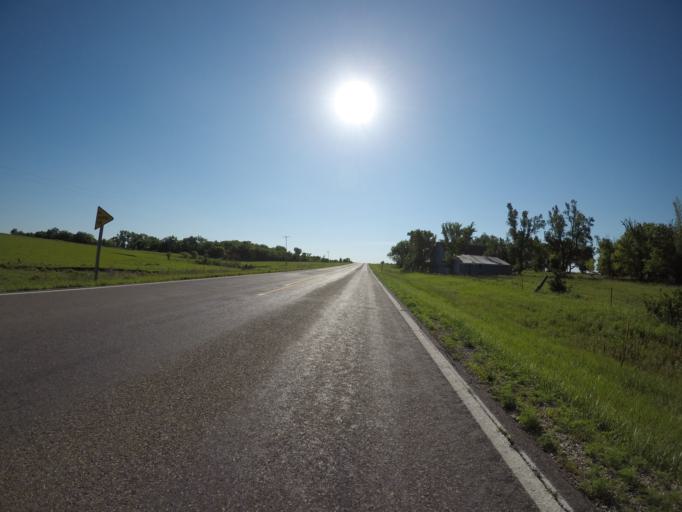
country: US
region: Kansas
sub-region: Lyon County
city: Emporia
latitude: 38.6589
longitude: -96.2226
